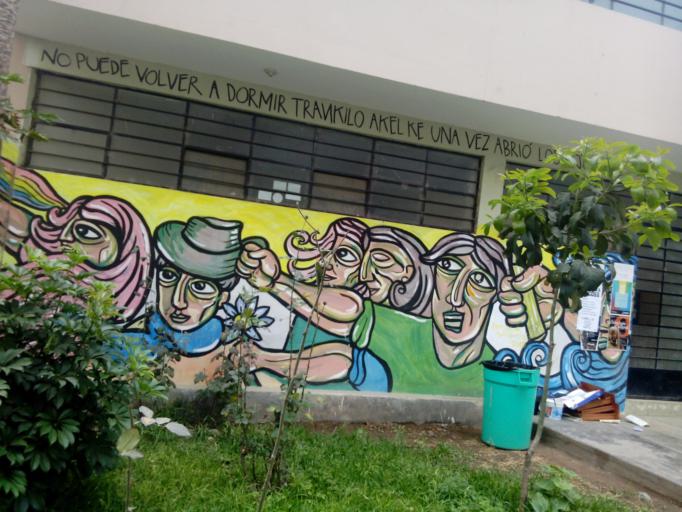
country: PE
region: Callao
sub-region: Callao
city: Callao
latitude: -12.0582
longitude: -77.0824
